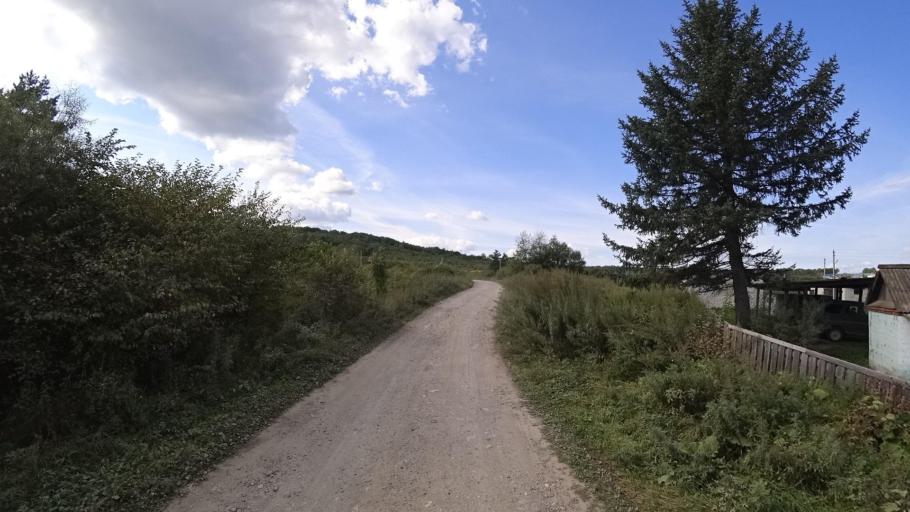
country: RU
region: Jewish Autonomous Oblast
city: Birakan
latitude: 49.0024
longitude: 131.7380
